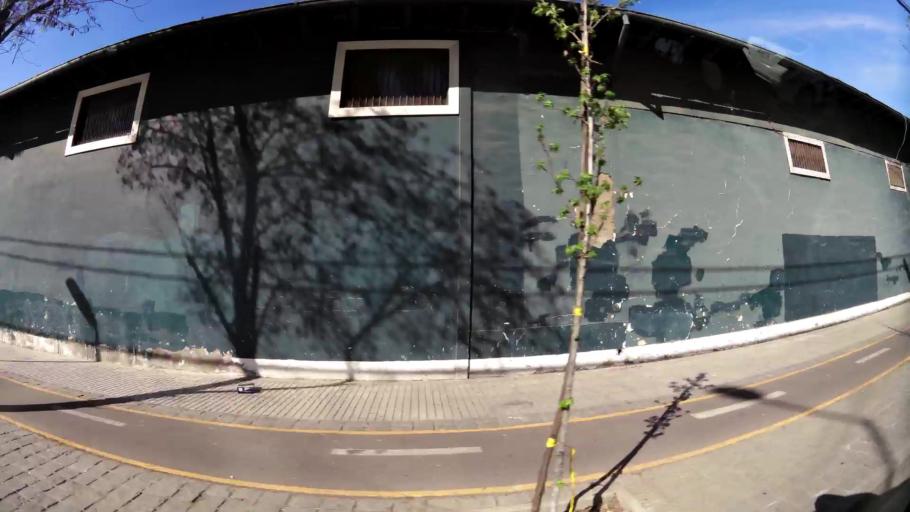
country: CL
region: Santiago Metropolitan
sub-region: Provincia de Santiago
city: Santiago
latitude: -33.4581
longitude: -70.6393
